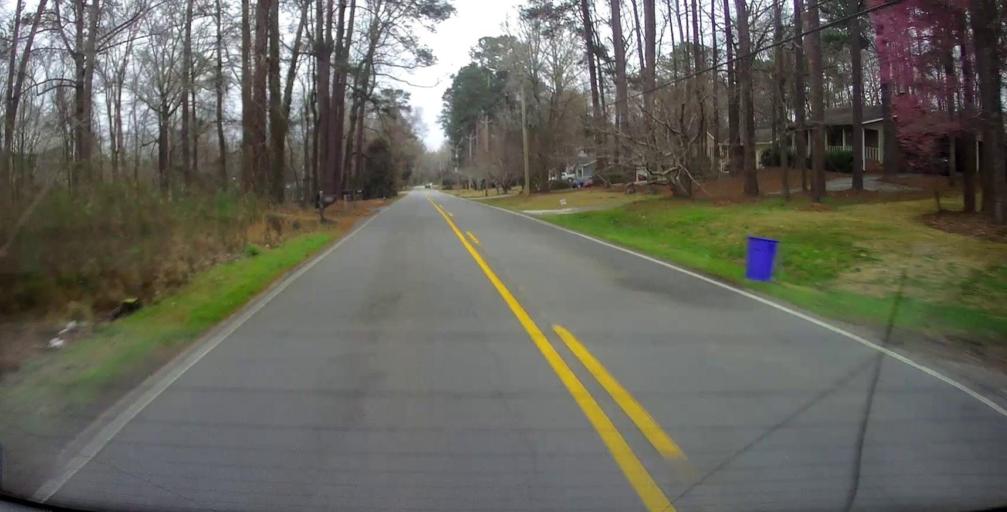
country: US
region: Georgia
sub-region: Bibb County
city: Macon
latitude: 32.8954
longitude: -83.7312
